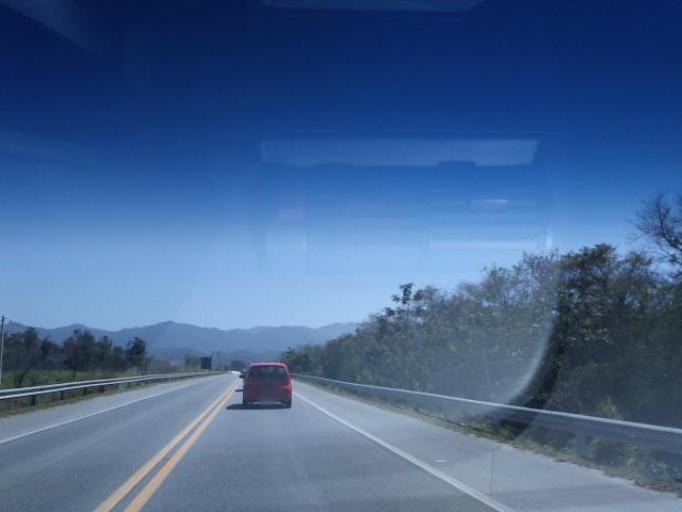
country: BR
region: Sao Paulo
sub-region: Taubate
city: Taubate
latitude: -23.0004
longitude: -45.6399
